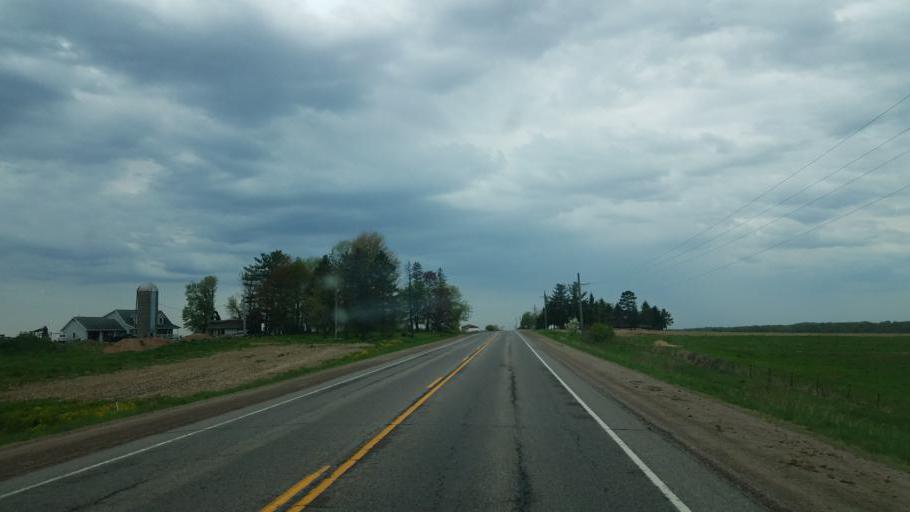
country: US
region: Wisconsin
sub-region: Marathon County
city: Spencer
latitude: 44.5980
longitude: -90.3668
